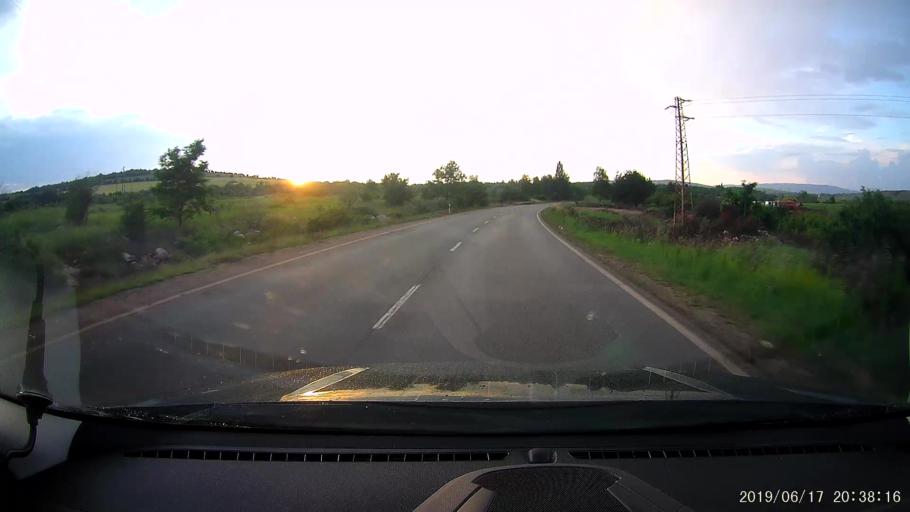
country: BG
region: Sofiya
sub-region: Obshtina Slivnitsa
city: Slivnitsa
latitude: 42.8698
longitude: 23.0200
